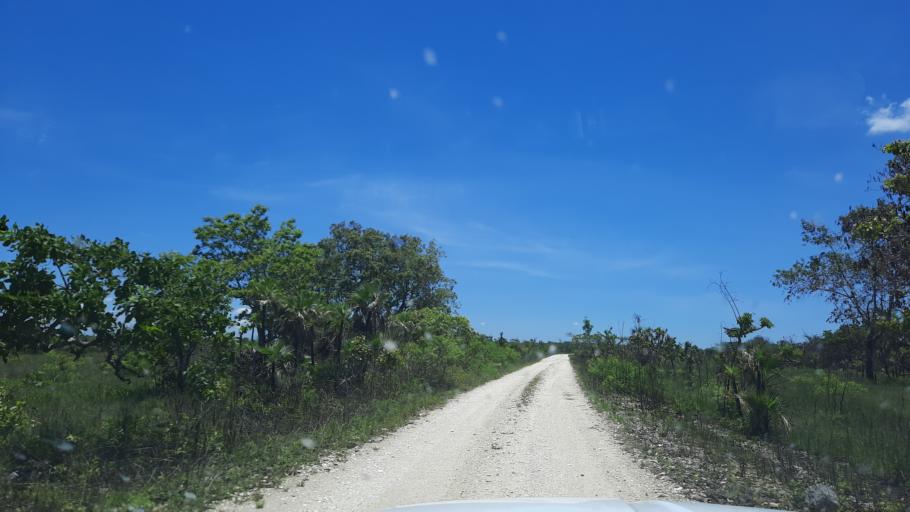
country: BZ
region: Cayo
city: Belmopan
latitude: 17.3863
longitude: -88.4942
